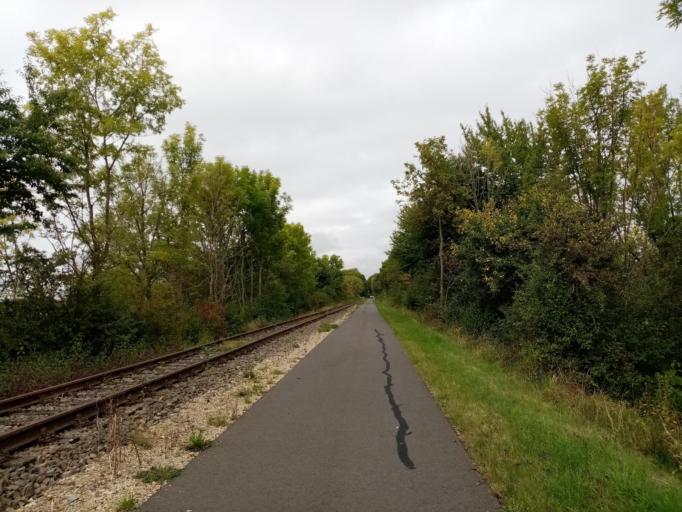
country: DE
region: Thuringia
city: Dingelstadt
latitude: 51.3013
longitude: 10.3071
